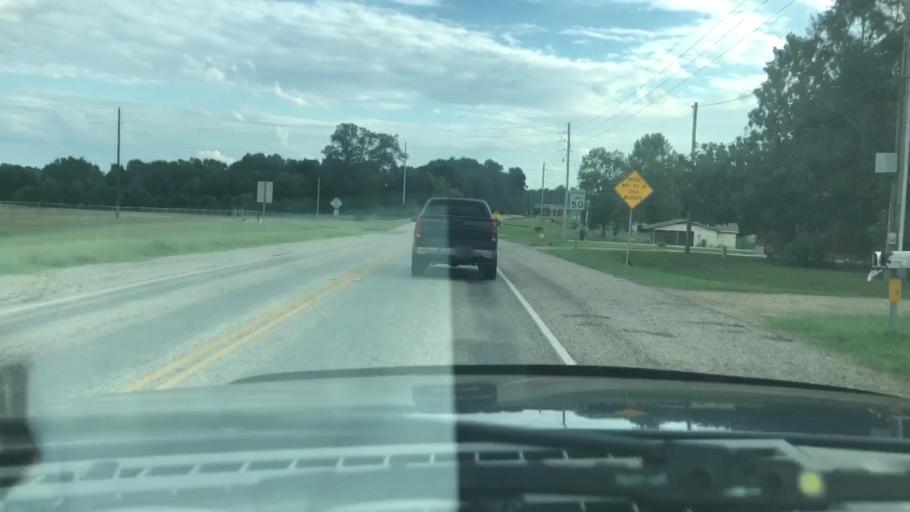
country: US
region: Texas
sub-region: Bowie County
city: Texarkana
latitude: 33.3910
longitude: -94.0656
